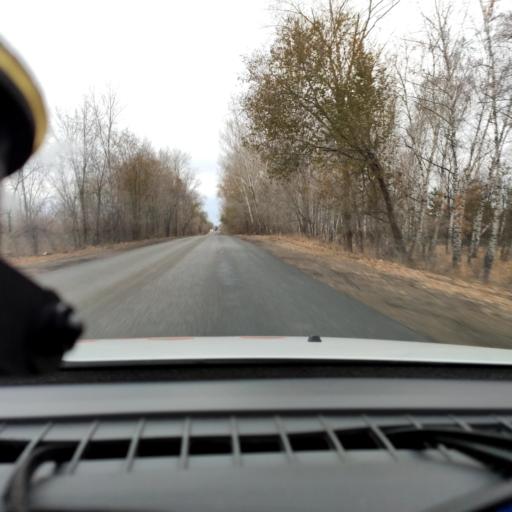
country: RU
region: Samara
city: Samara
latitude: 53.1209
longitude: 50.2324
